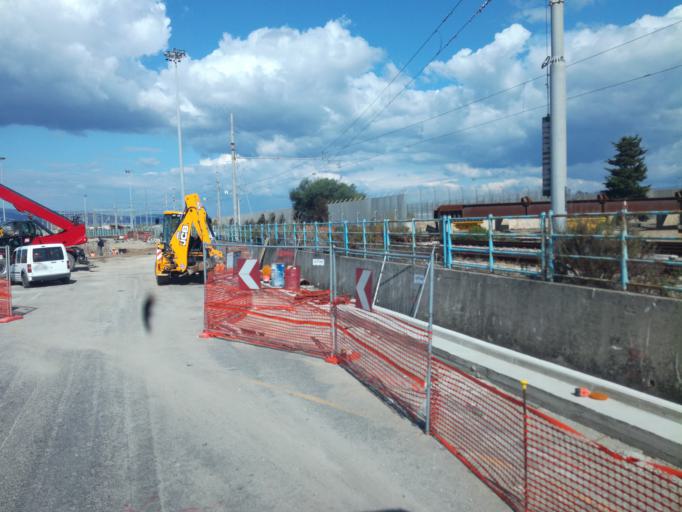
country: IT
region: Calabria
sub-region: Provincia di Reggio Calabria
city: San Ferdinando
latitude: 38.4694
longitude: 15.9197
